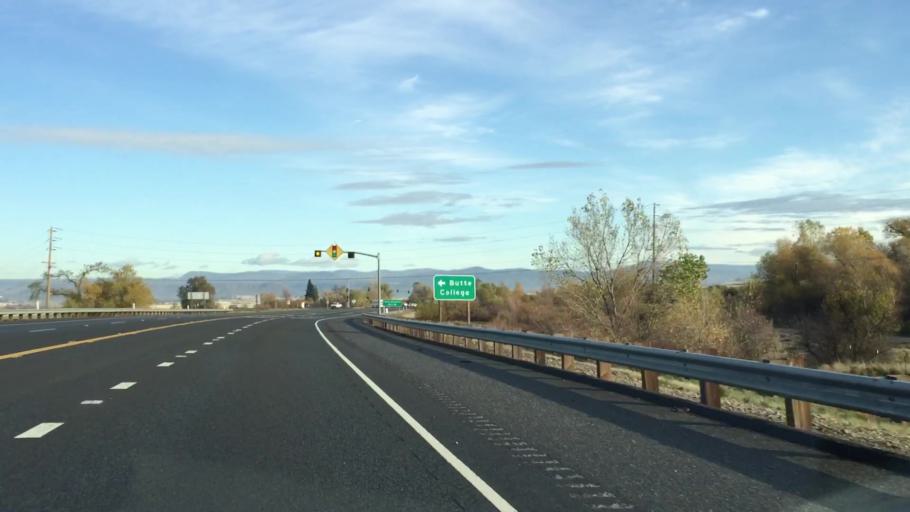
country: US
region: California
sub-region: Butte County
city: Thermalito
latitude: 39.5997
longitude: -121.6199
